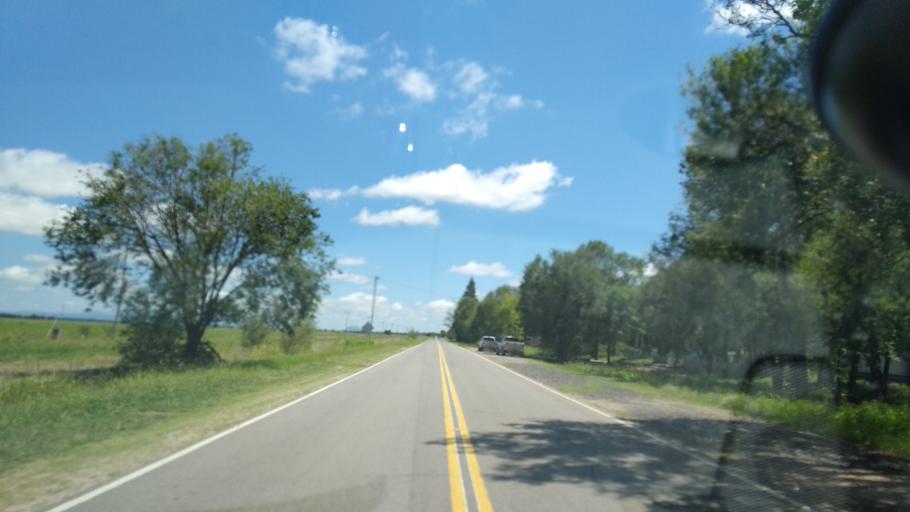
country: AR
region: Cordoba
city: Villa Cura Brochero
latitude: -31.5825
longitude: -65.1118
